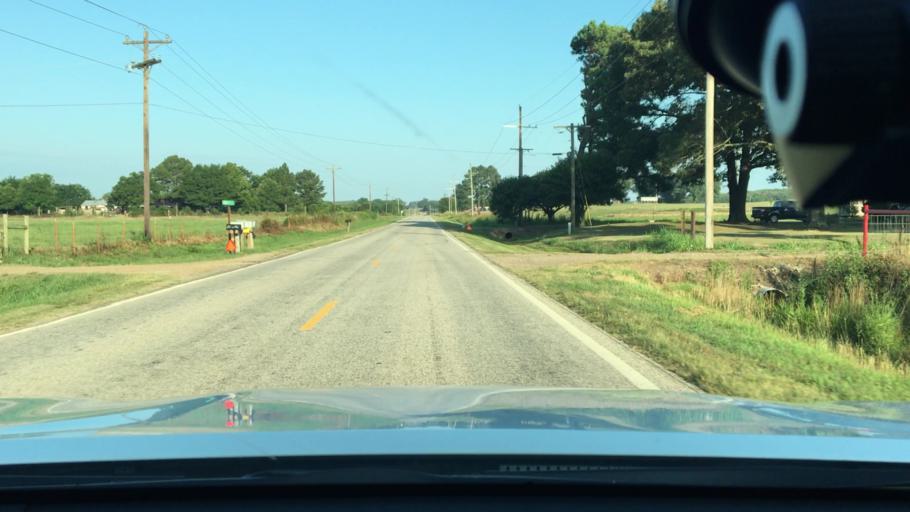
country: US
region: Arkansas
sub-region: Johnson County
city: Coal Hill
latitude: 35.3373
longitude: -93.6182
